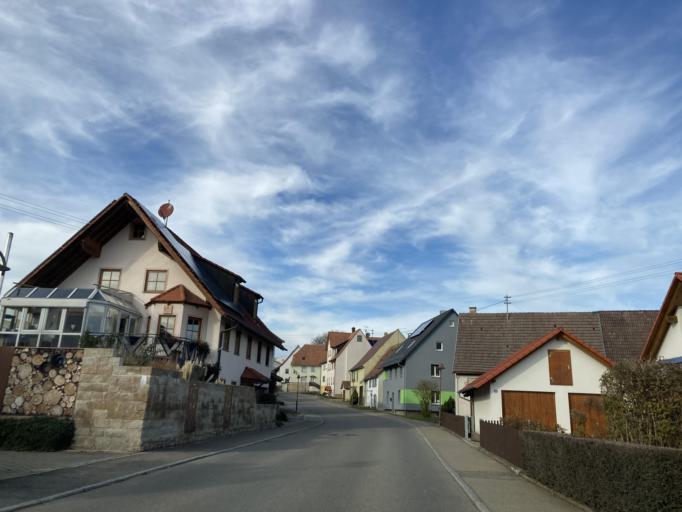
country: DE
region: Baden-Wuerttemberg
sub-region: Tuebingen Region
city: Haigerloch
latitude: 48.4301
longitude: 8.8190
